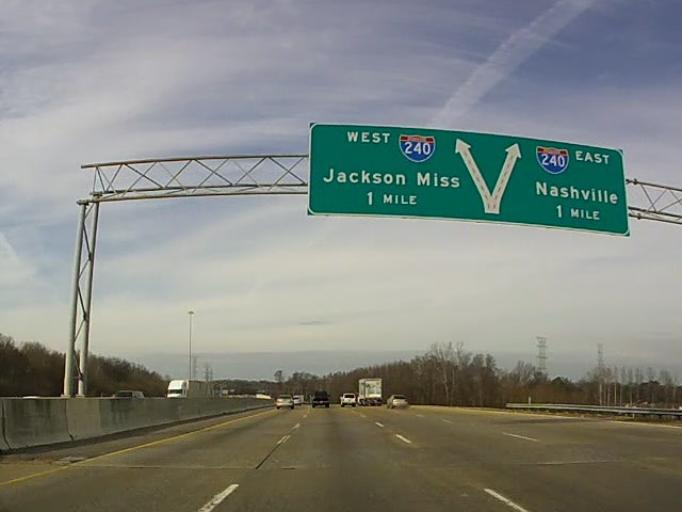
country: US
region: Tennessee
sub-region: Shelby County
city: Germantown
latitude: 35.0757
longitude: -89.8630
